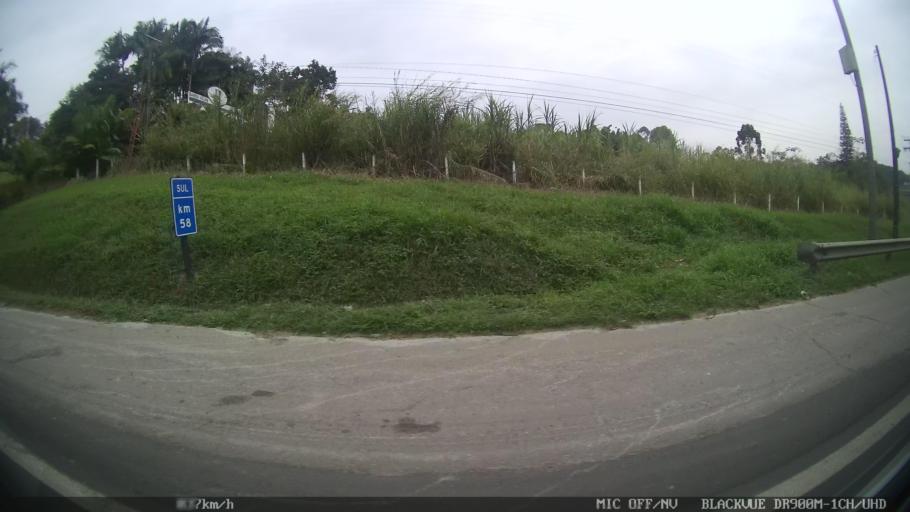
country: BR
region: Santa Catarina
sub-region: Joinville
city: Joinville
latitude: -26.4405
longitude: -48.8011
